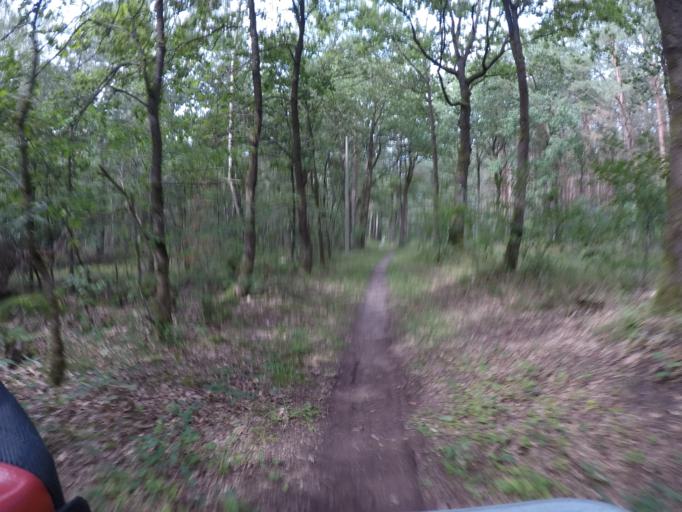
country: DE
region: Lower Saxony
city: Wittorf
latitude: 53.3299
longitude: 10.3993
